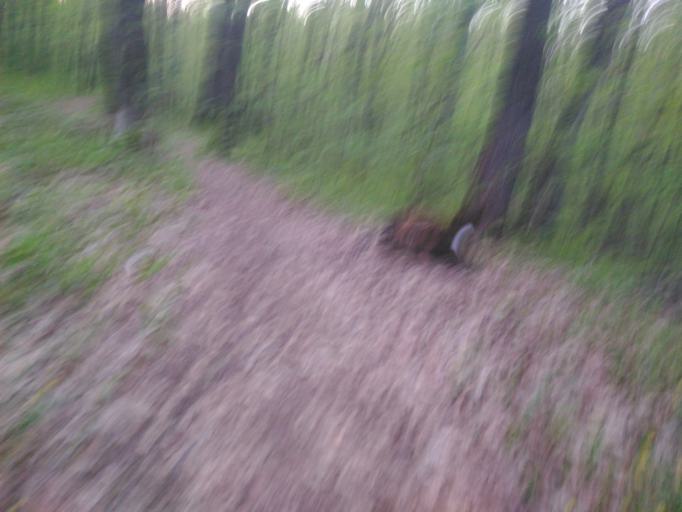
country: RU
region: Ulyanovsk
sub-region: Ulyanovskiy Rayon
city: Ulyanovsk
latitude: 54.2715
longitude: 48.3387
